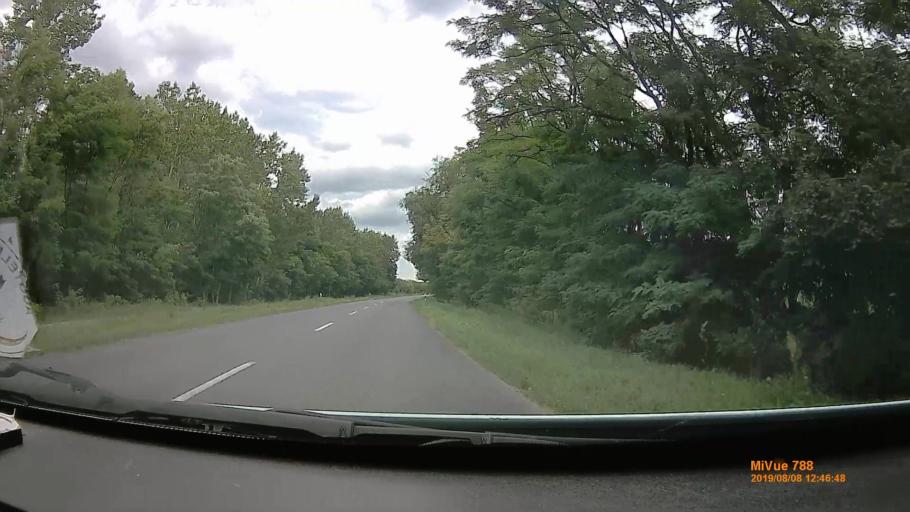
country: HU
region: Szabolcs-Szatmar-Bereg
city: Hodasz
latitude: 47.8995
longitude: 22.2254
